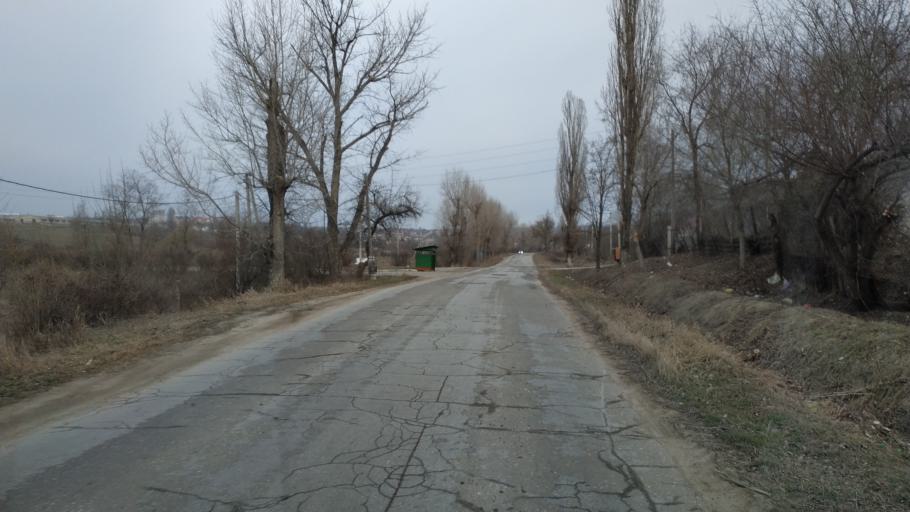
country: MD
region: Chisinau
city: Vatra
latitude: 47.0801
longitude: 28.7695
